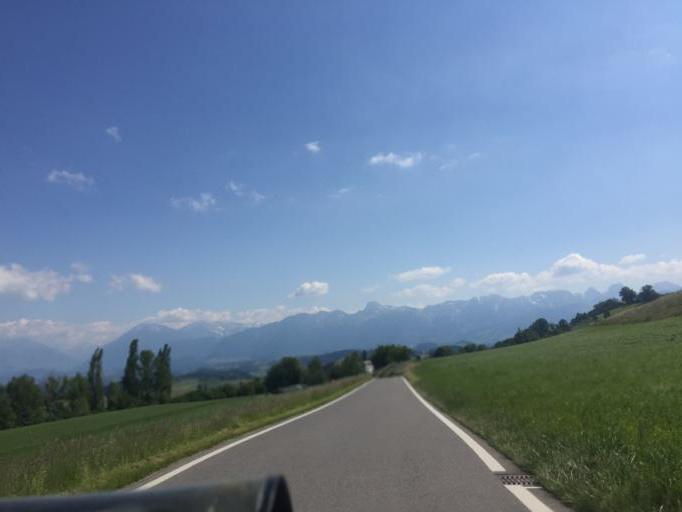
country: CH
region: Bern
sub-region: Bern-Mittelland District
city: Munsingen
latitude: 46.8484
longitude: 7.5451
